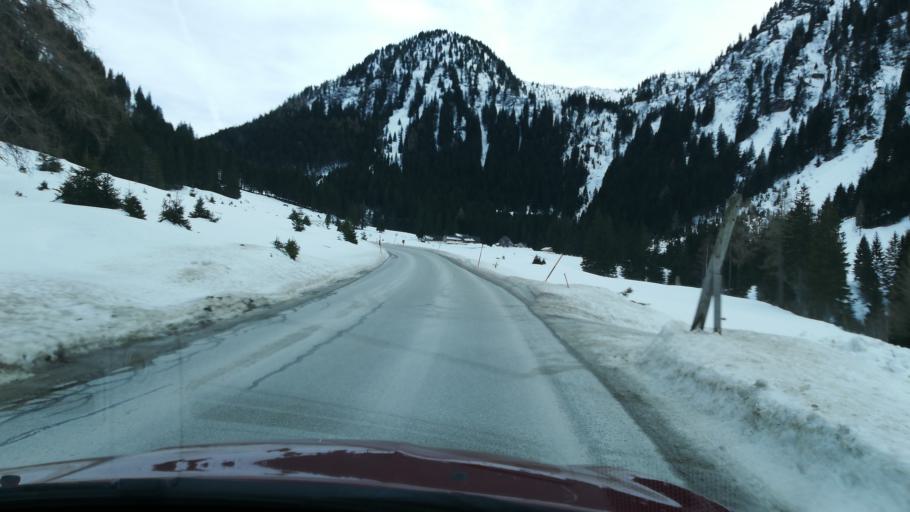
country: AT
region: Styria
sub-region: Politischer Bezirk Liezen
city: Donnersbach
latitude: 47.4152
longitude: 14.1759
